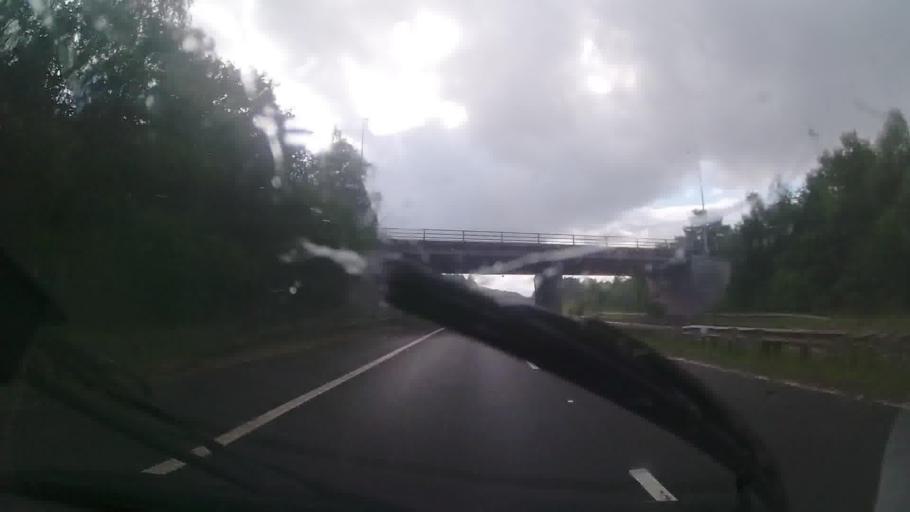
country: GB
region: England
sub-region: Shropshire
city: Hadley
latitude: 52.6887
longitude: -2.4874
